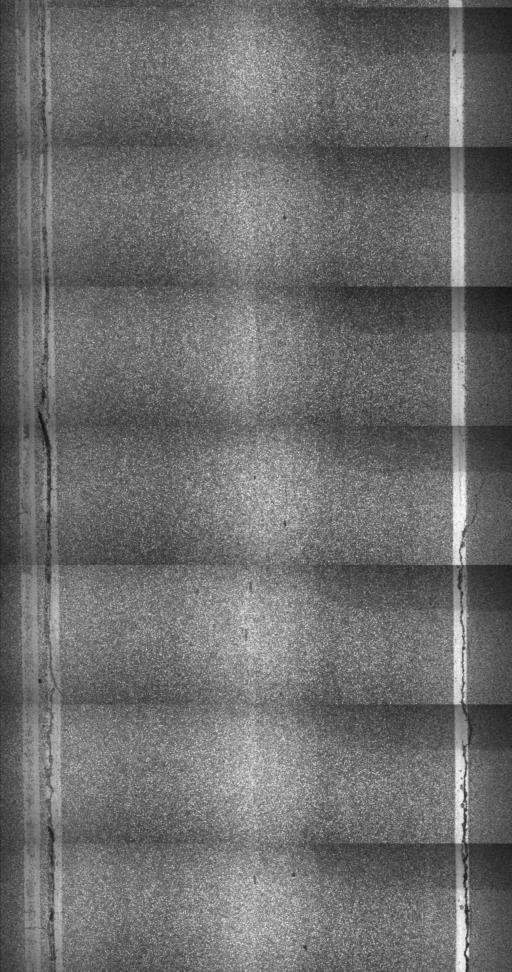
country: US
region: Vermont
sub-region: Washington County
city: Barre
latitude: 44.2588
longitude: -72.4862
